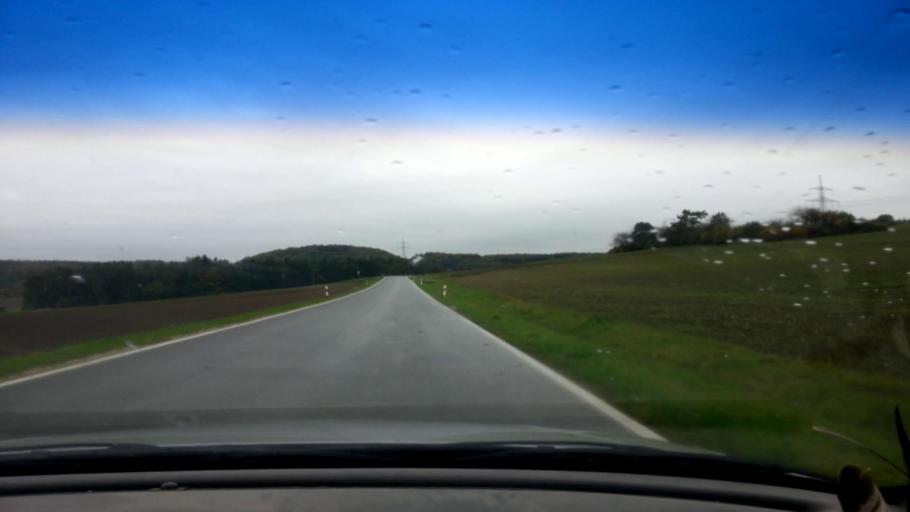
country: DE
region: Bavaria
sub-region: Upper Franconia
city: Poxdorf
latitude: 49.8852
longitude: 11.1112
